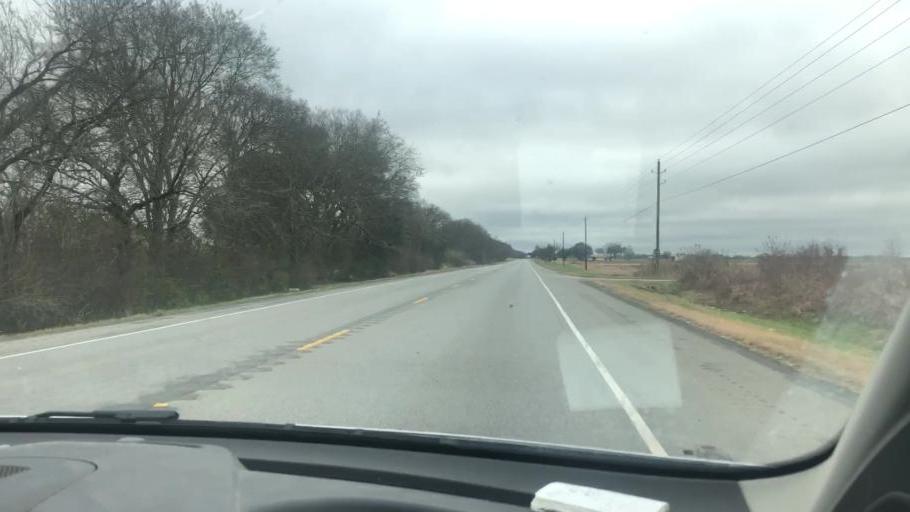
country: US
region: Texas
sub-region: Matagorda County
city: Bay City
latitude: 29.0742
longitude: -95.9722
